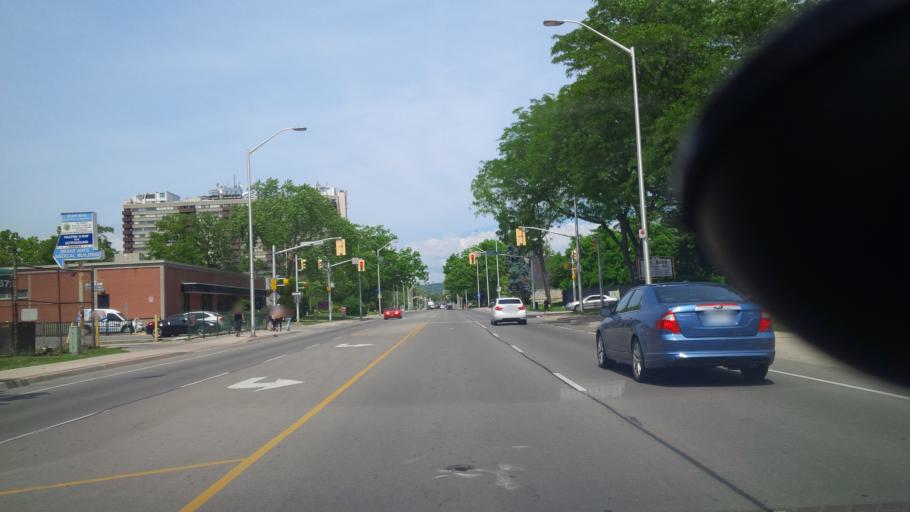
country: CA
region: Ontario
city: Burlington
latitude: 43.3309
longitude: -79.8053
